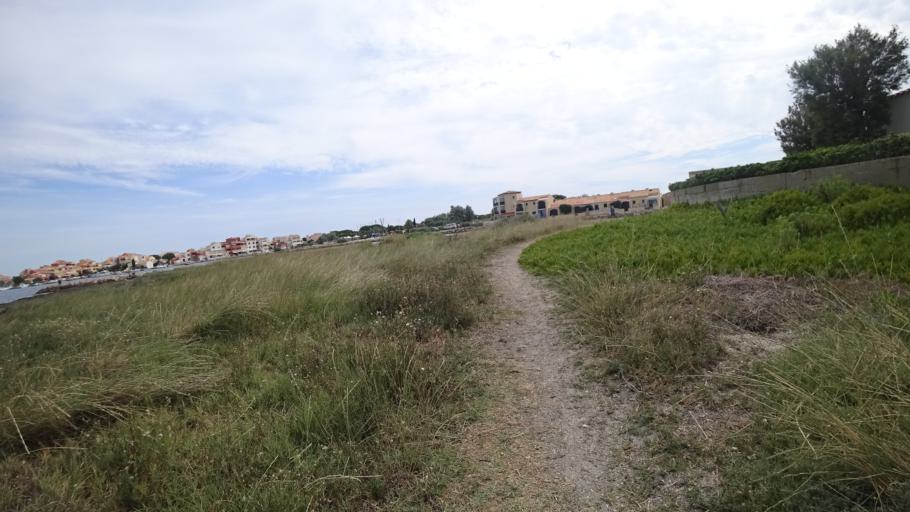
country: FR
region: Languedoc-Roussillon
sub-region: Departement des Pyrenees-Orientales
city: Le Barcares
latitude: 42.8089
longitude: 3.0267
